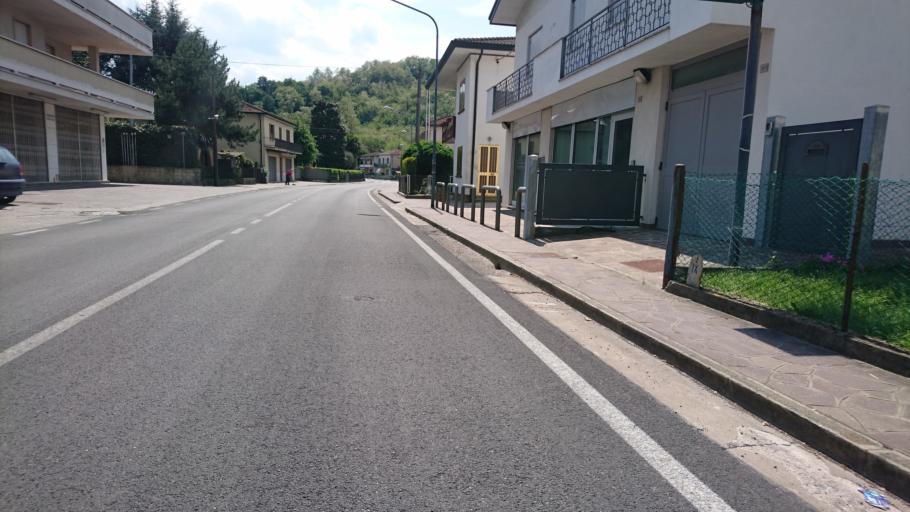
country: IT
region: Veneto
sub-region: Provincia di Padova
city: Montemerlo
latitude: 45.3813
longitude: 11.7053
